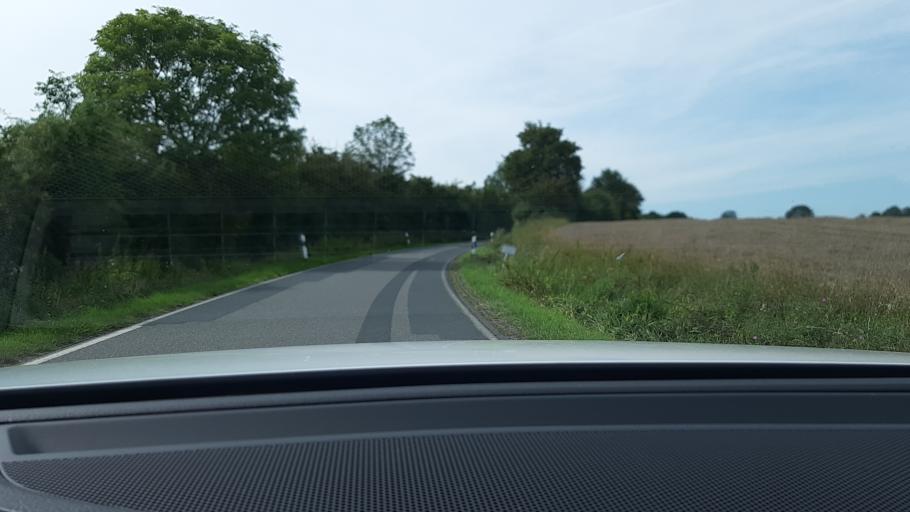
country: DE
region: Schleswig-Holstein
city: Heidekamp
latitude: 53.8677
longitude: 10.4959
